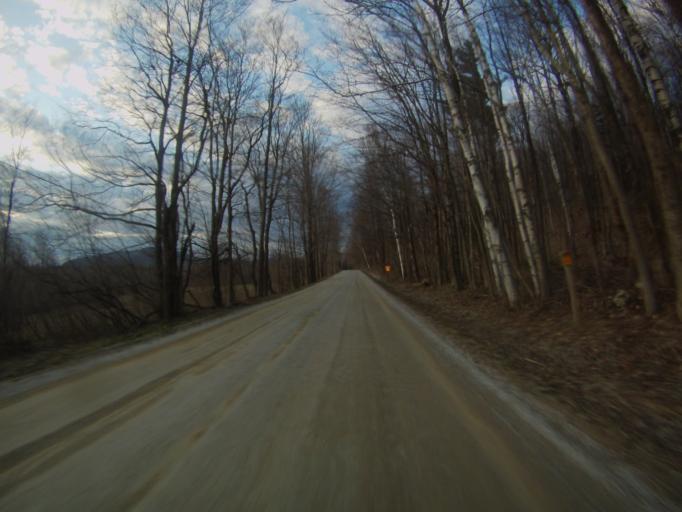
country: US
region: Vermont
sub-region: Rutland County
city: Brandon
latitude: 43.8794
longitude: -73.0124
